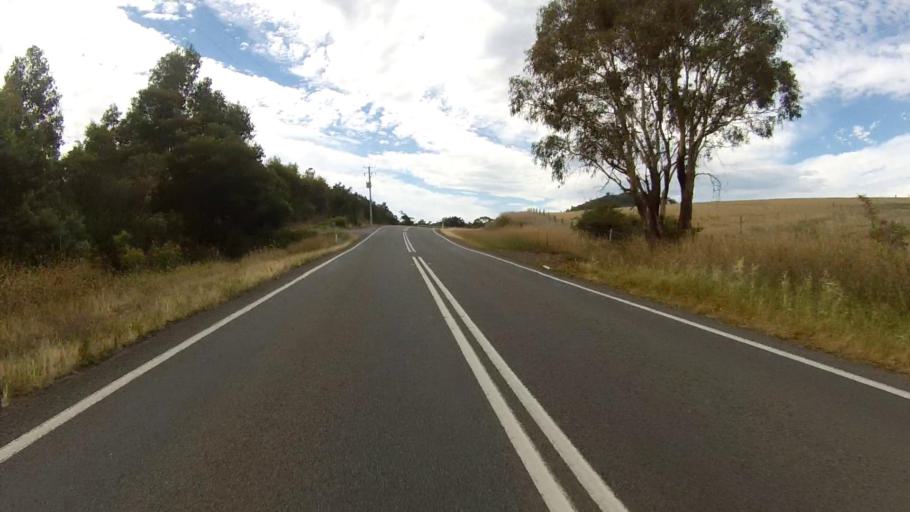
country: AU
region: Tasmania
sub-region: Sorell
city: Sorell
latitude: -42.6967
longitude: 147.4817
